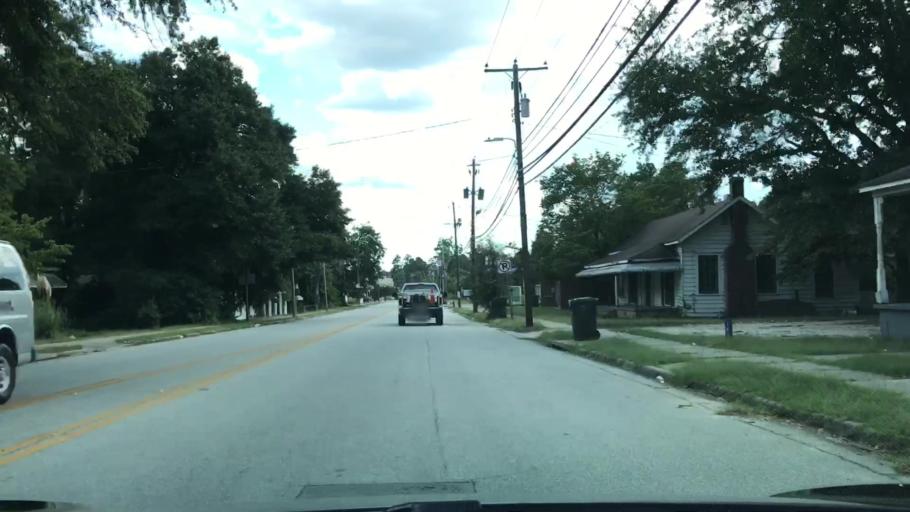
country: US
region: Georgia
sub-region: Jefferson County
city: Wadley
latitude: 32.8658
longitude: -82.4047
